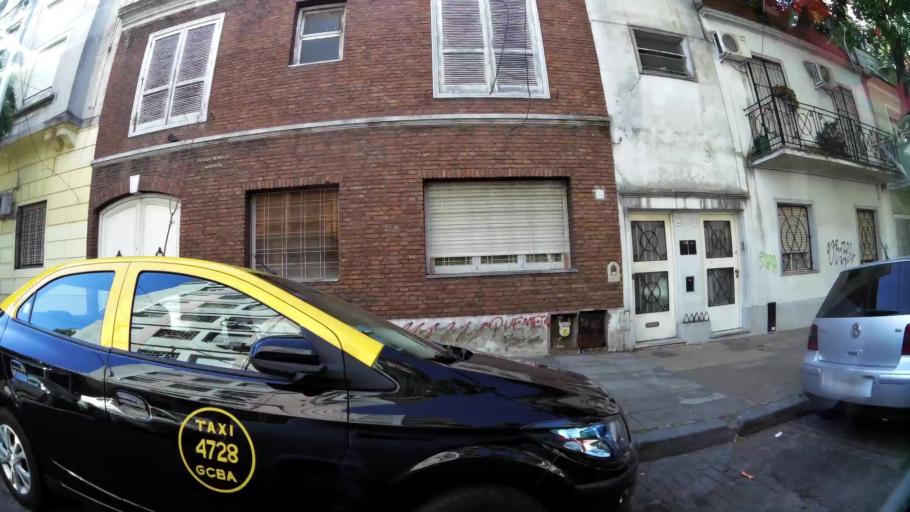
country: AR
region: Buenos Aires F.D.
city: Villa Santa Rita
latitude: -34.6203
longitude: -58.4608
